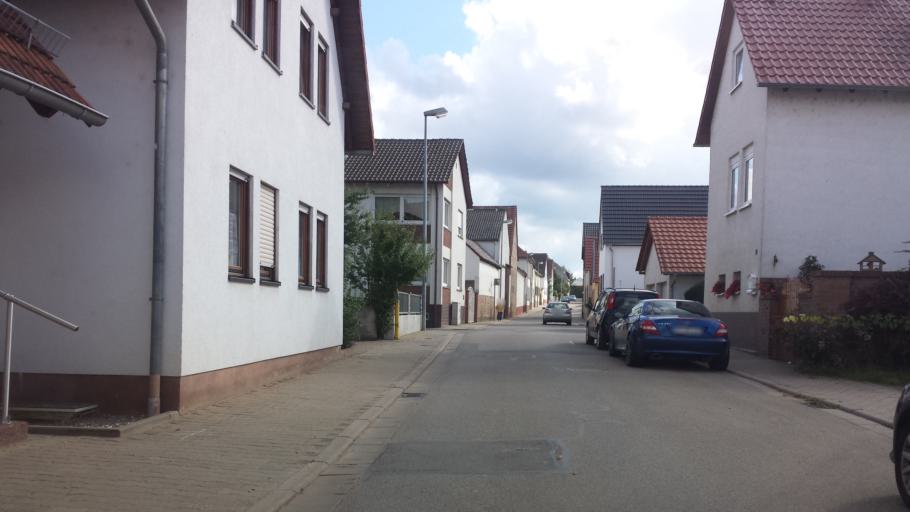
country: DE
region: Rheinland-Pfalz
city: Hochdorf-Assenheim
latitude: 49.4225
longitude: 8.2844
